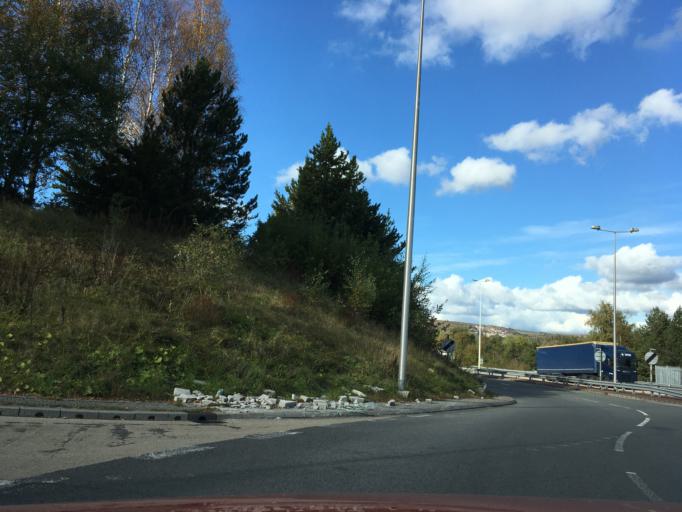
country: GB
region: Wales
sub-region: Merthyr Tydfil County Borough
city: Merthyr Tydfil
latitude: 51.7503
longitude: -3.3975
